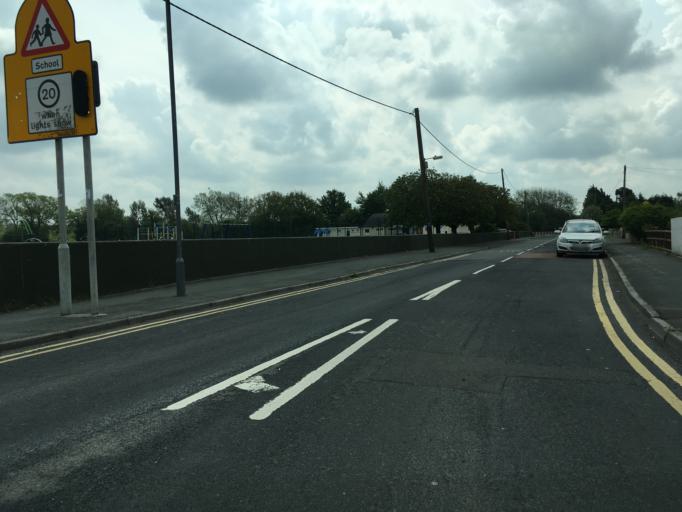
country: GB
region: England
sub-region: South Gloucestershire
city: Severn Beach
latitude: 51.5602
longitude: -2.6627
